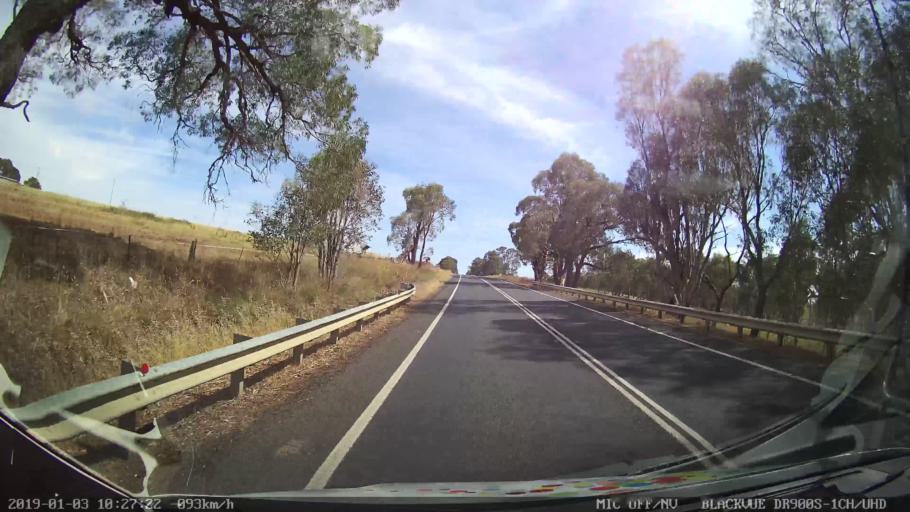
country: AU
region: New South Wales
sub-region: Young
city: Young
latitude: -34.4029
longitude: 148.2585
